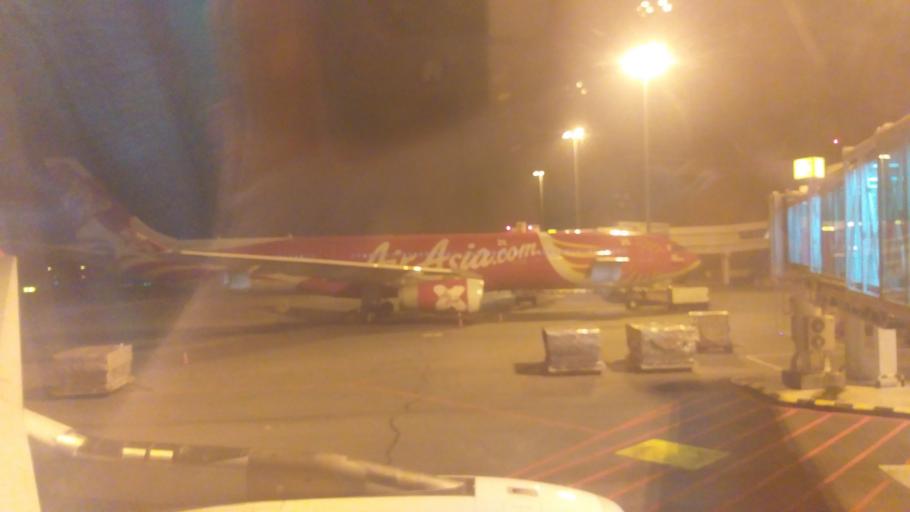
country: MY
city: Sungai Pelek New Village
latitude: 2.7365
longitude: 101.6854
